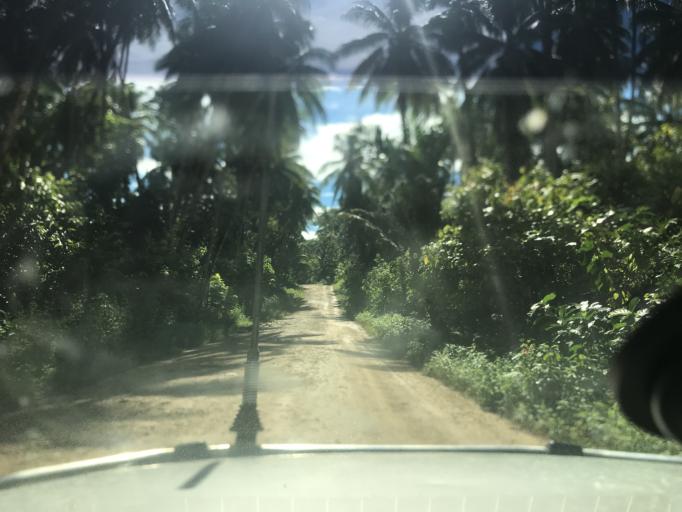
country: SB
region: Malaita
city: Auki
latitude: -8.3562
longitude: 160.6561
